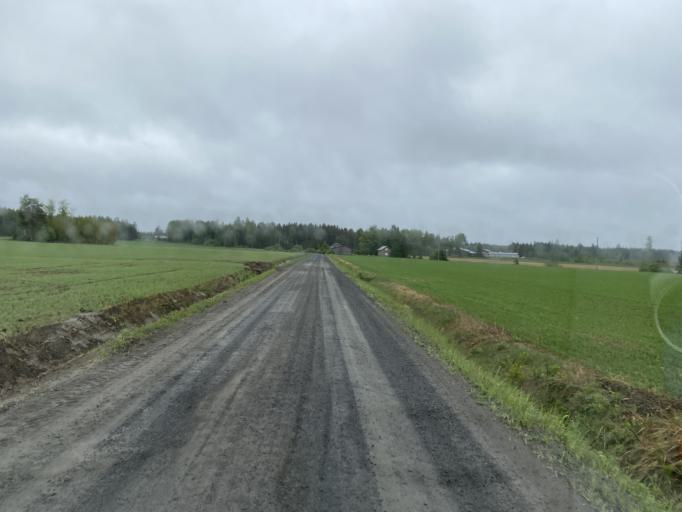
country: FI
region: Haeme
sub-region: Forssa
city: Forssa
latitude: 60.9361
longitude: 23.5804
